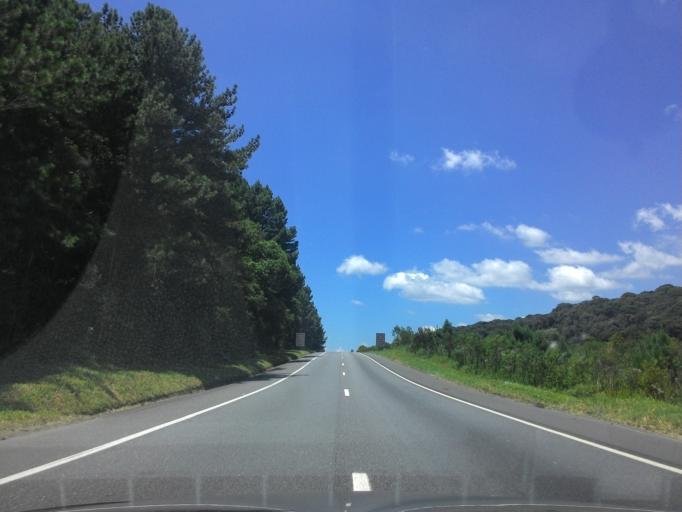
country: BR
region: Sao Paulo
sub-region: Cajati
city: Cajati
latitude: -24.9682
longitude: -48.4417
